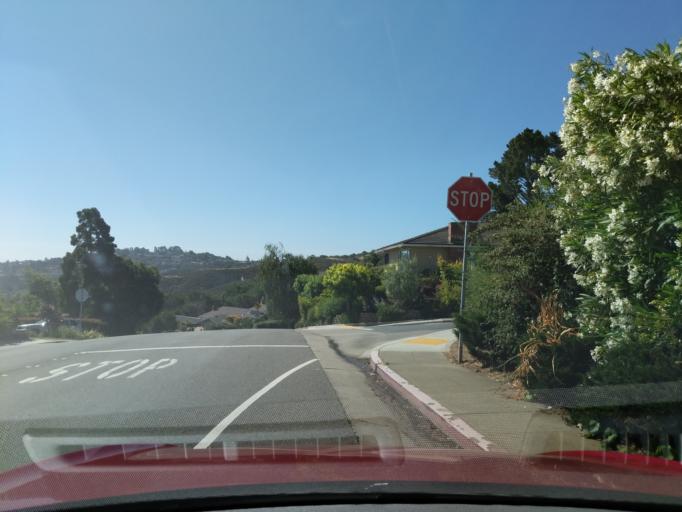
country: US
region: California
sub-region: San Mateo County
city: Highlands-Baywood Park
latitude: 37.5298
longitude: -122.3218
